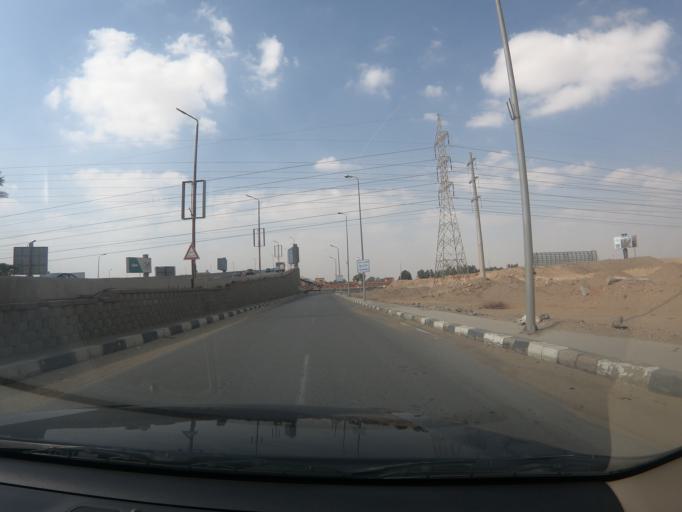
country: EG
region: Muhafazat al Qalyubiyah
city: Al Khankah
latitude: 30.0812
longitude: 31.4713
